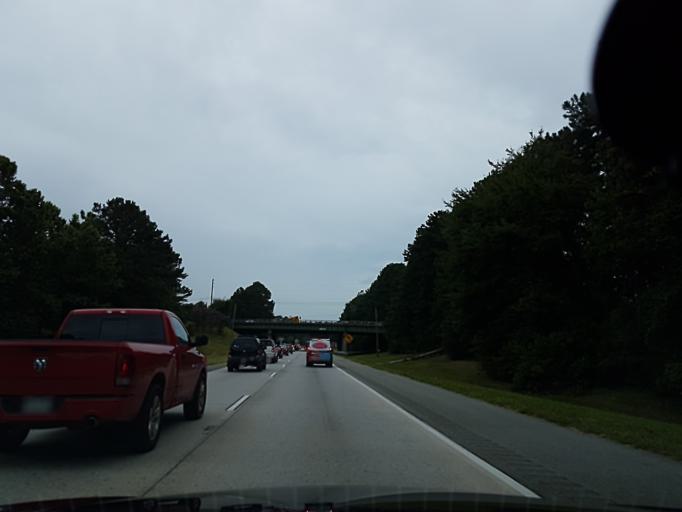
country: US
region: Georgia
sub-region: DeKalb County
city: Scottdale
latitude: 33.8086
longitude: -84.2723
